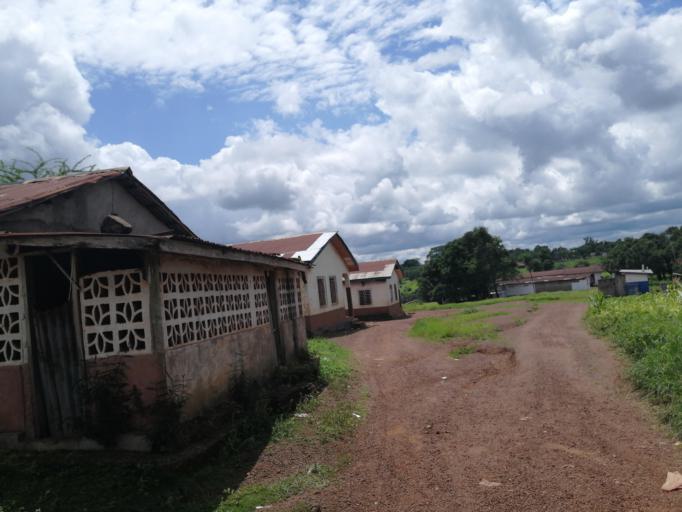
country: SL
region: Northern Province
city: Port Loko
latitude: 8.7685
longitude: -12.7837
